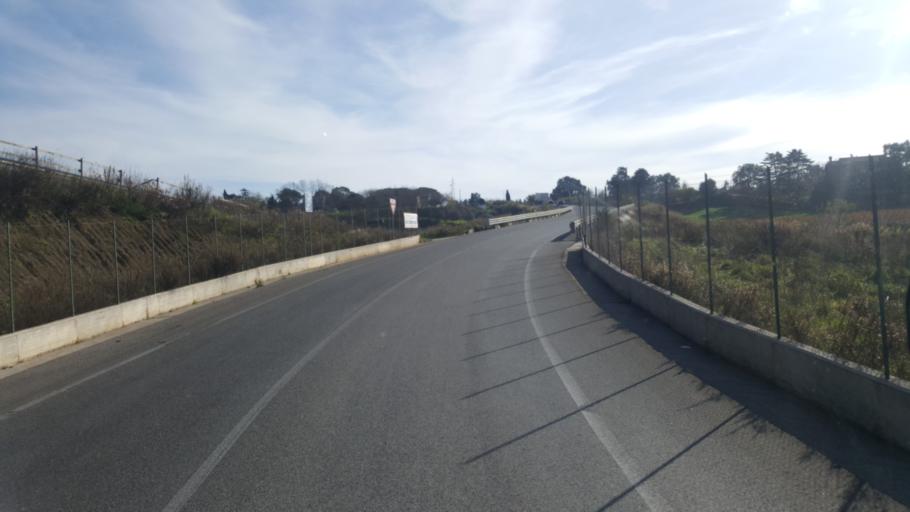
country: IT
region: Latium
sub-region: Citta metropolitana di Roma Capitale
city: Mantiglia di Ardea
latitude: 41.6729
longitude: 12.6338
